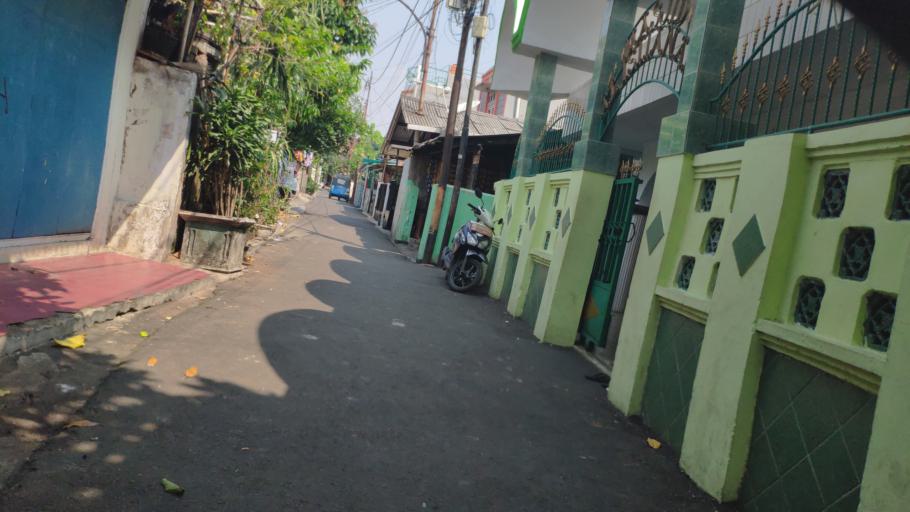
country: ID
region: Jakarta Raya
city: Jakarta
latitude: -6.2551
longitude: 106.7935
